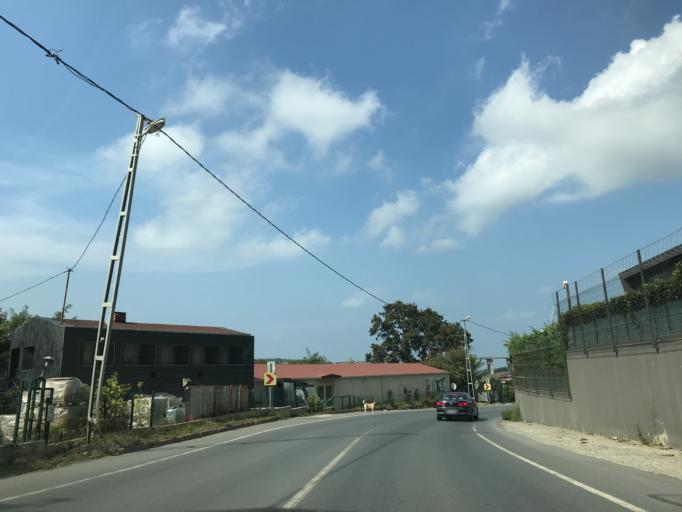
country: TR
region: Istanbul
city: Arikoey
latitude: 41.2147
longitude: 29.0340
